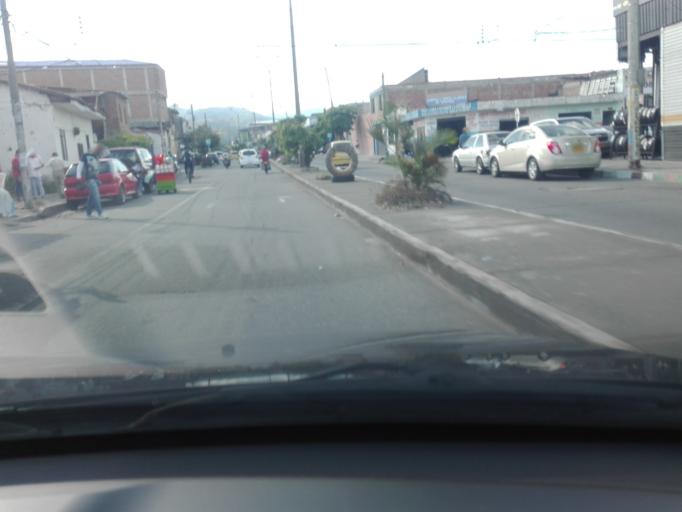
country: CO
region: Valle del Cauca
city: Cali
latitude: 3.4406
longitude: -76.5157
